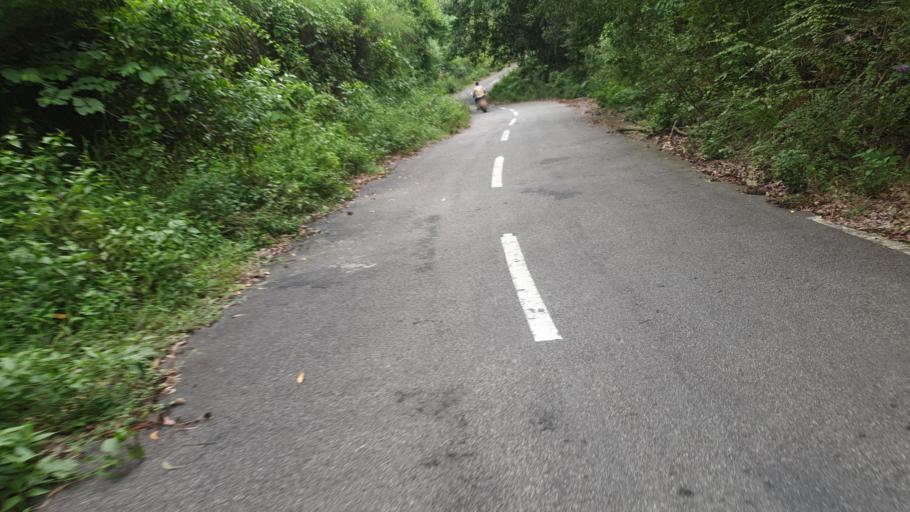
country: IN
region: Kerala
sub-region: Thiruvananthapuram
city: Nedumangad
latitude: 8.6306
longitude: 77.1238
